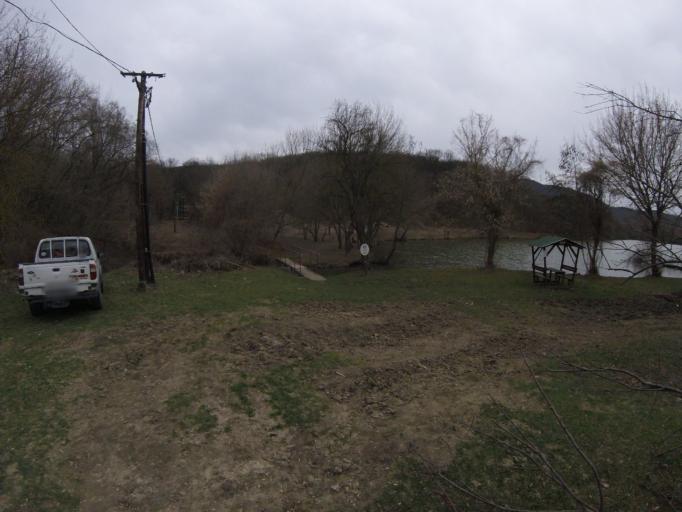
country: HU
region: Pest
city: Szob
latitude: 47.8035
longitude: 18.8074
